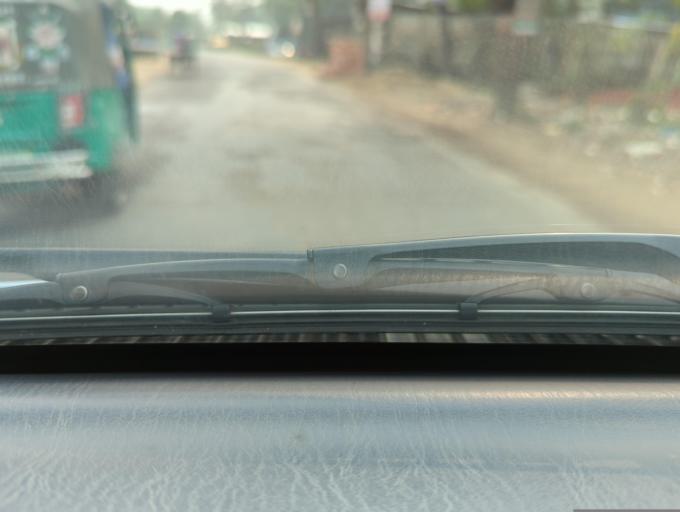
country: BD
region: Sylhet
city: Maulavi Bazar
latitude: 24.4904
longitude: 91.7474
